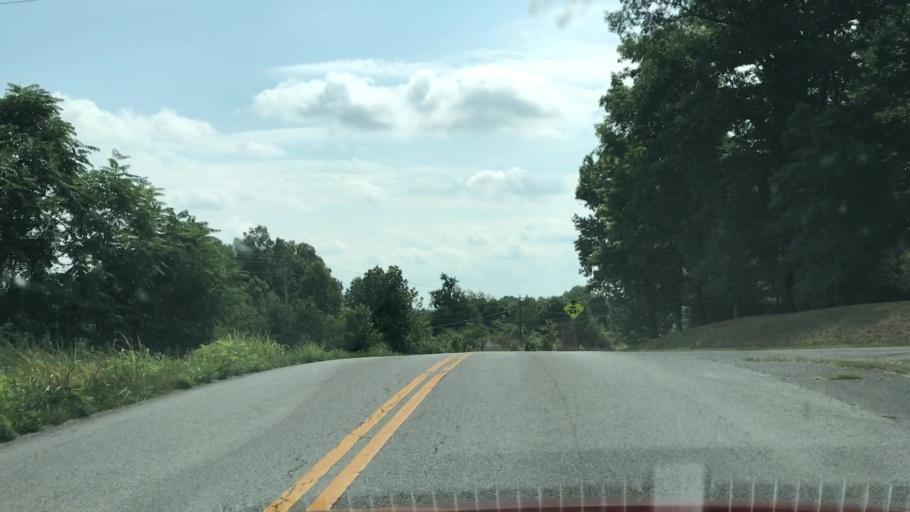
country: US
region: Kentucky
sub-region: Barren County
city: Glasgow
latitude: 36.8994
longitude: -85.8618
